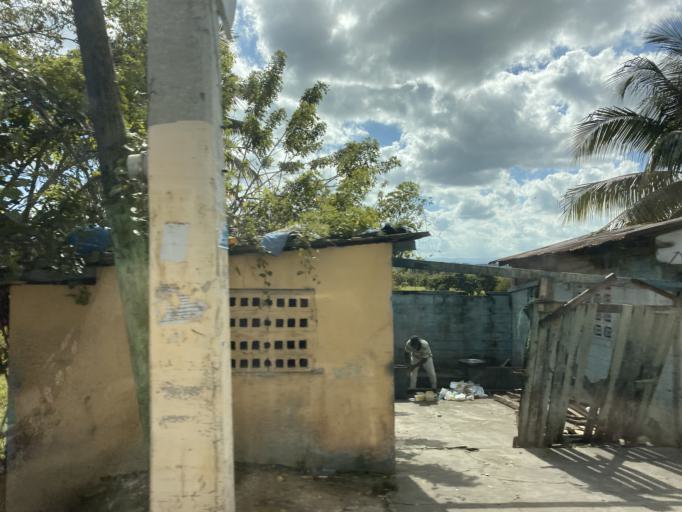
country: DO
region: Espaillat
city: Jamao al Norte
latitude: 19.6712
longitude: -70.3718
